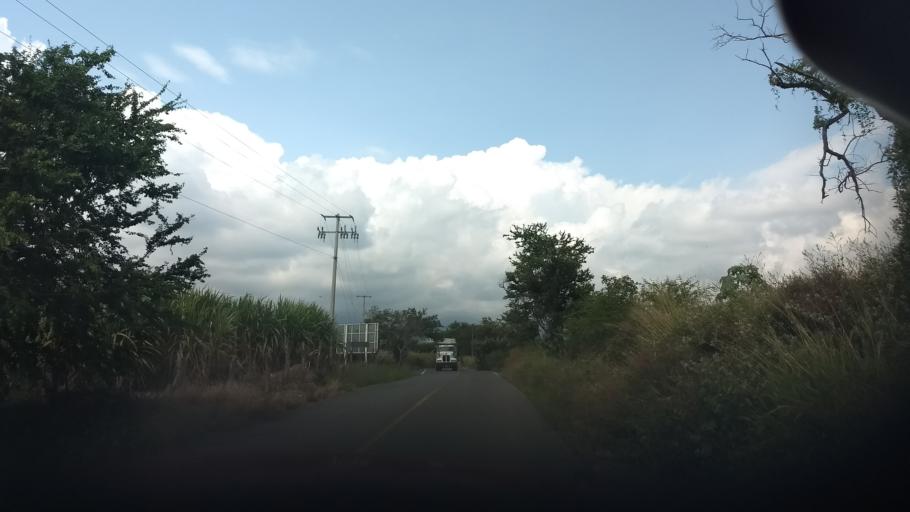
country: MX
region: Jalisco
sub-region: Tonila
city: San Marcos
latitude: 19.4317
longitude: -103.4929
